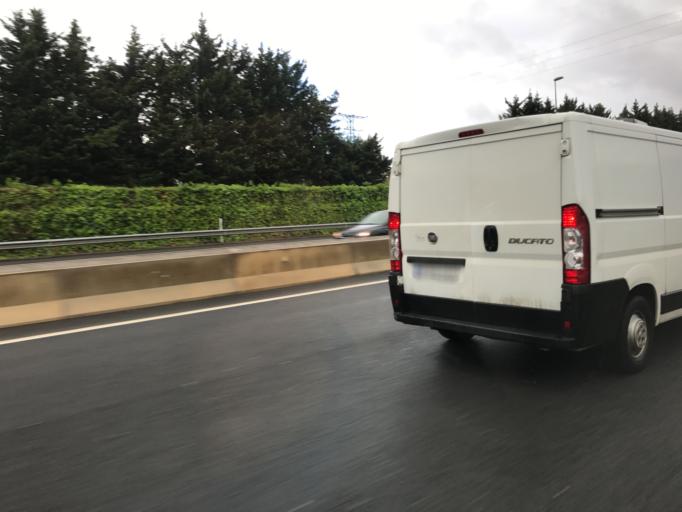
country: ES
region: Basque Country
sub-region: Bizkaia
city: Derio
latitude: 43.2936
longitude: -2.8816
